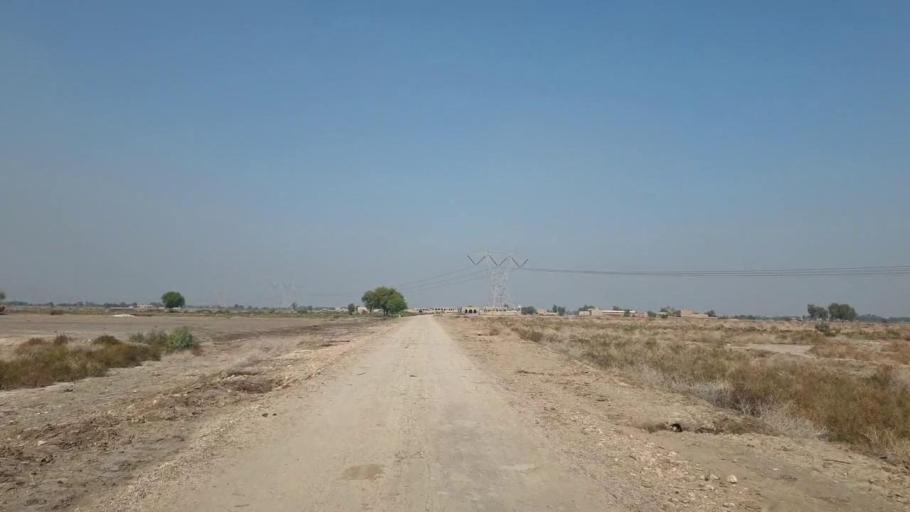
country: PK
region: Sindh
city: Sehwan
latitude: 26.4181
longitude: 67.8105
